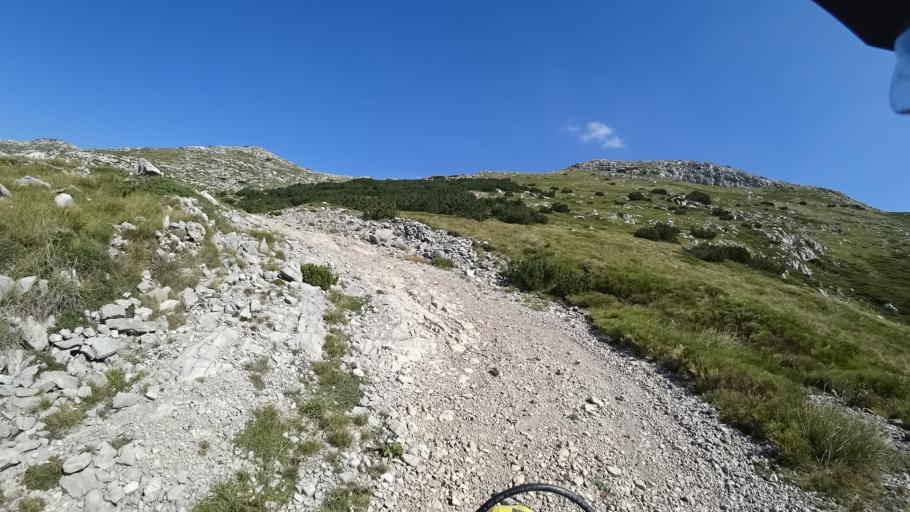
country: HR
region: Splitsko-Dalmatinska
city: Hrvace
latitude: 43.9331
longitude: 16.6013
